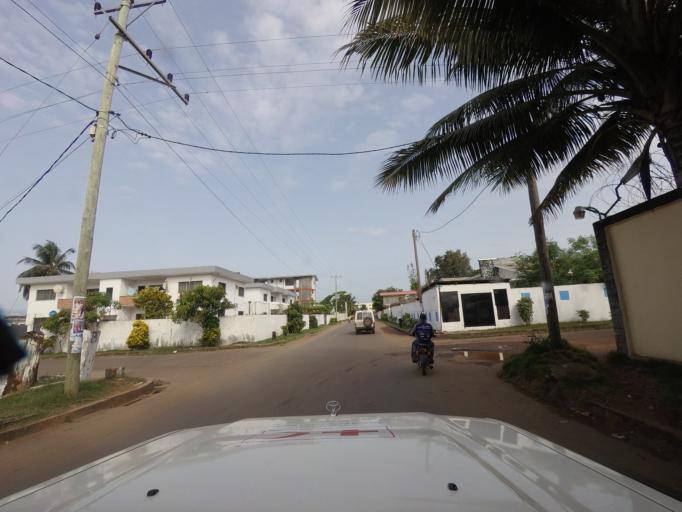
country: LR
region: Montserrado
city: Monrovia
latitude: 6.2918
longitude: -10.7846
